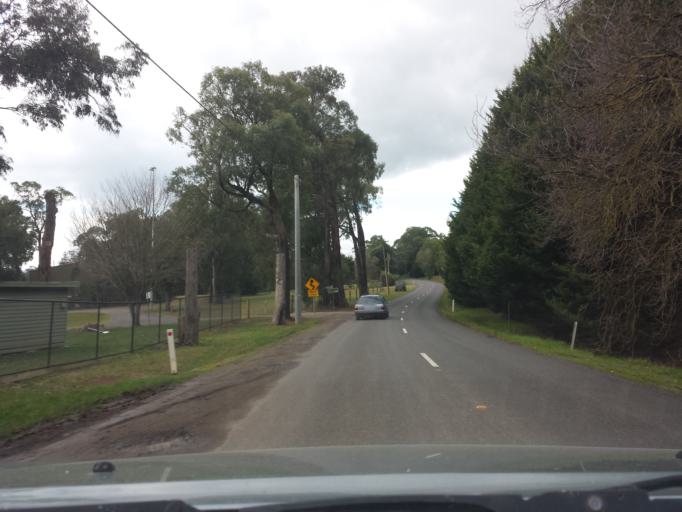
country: AU
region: Victoria
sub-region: Yarra Ranges
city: Macclesfield
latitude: -37.8161
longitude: 145.4590
